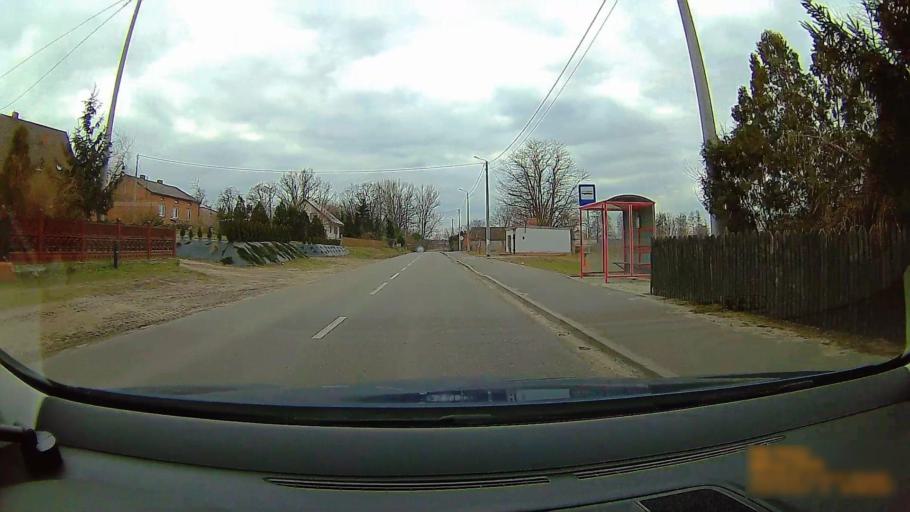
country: PL
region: Greater Poland Voivodeship
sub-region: Powiat koninski
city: Rzgow Pierwszy
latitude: 52.1703
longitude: 18.0867
